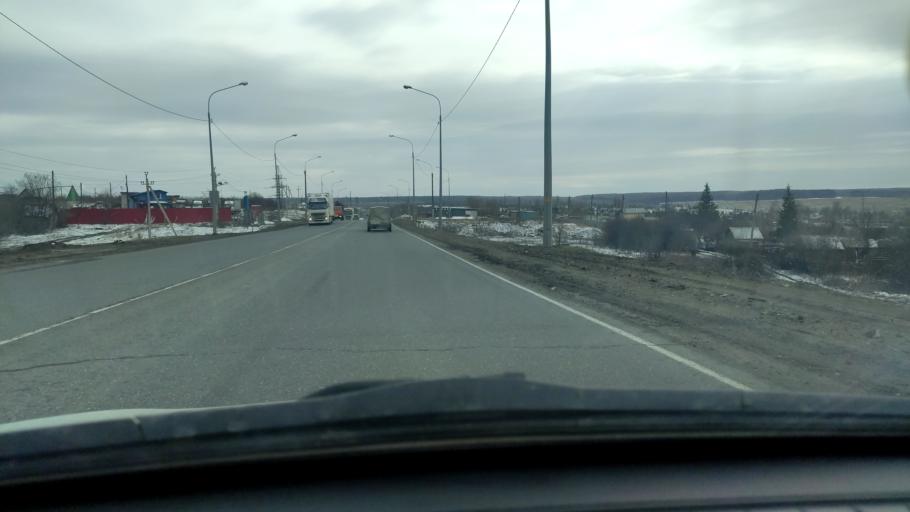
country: RU
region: Samara
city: Zhigulevsk
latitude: 53.3712
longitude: 49.4570
